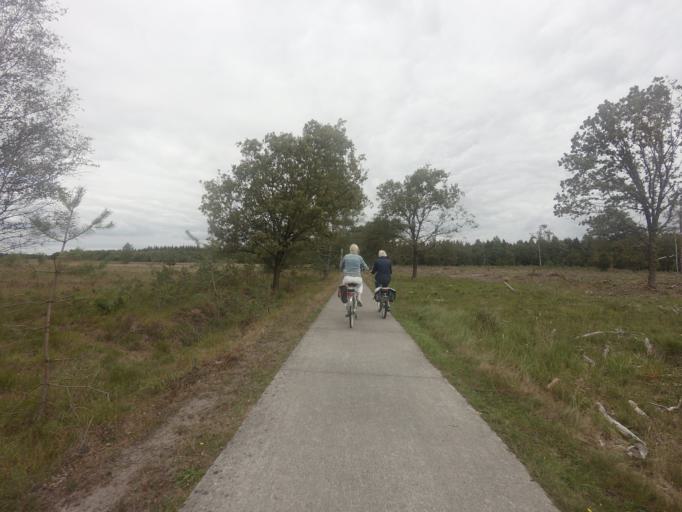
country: NL
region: Drenthe
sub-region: Gemeente Westerveld
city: Dwingeloo
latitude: 52.8876
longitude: 6.2915
